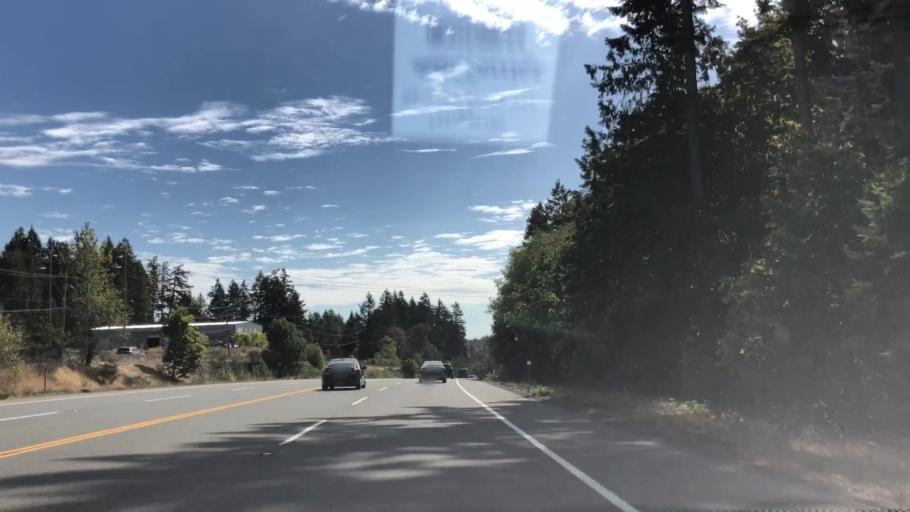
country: CA
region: British Columbia
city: Nanaimo
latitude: 49.1335
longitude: -123.8692
